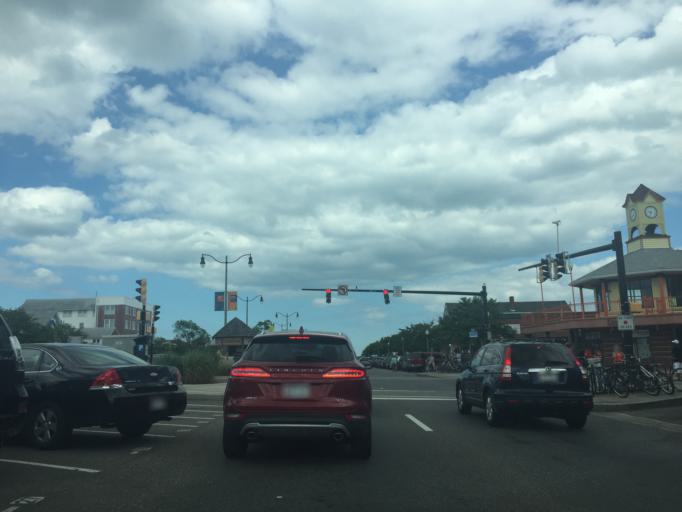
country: US
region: Delaware
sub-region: Sussex County
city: Rehoboth Beach
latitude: 38.7162
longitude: -75.0793
